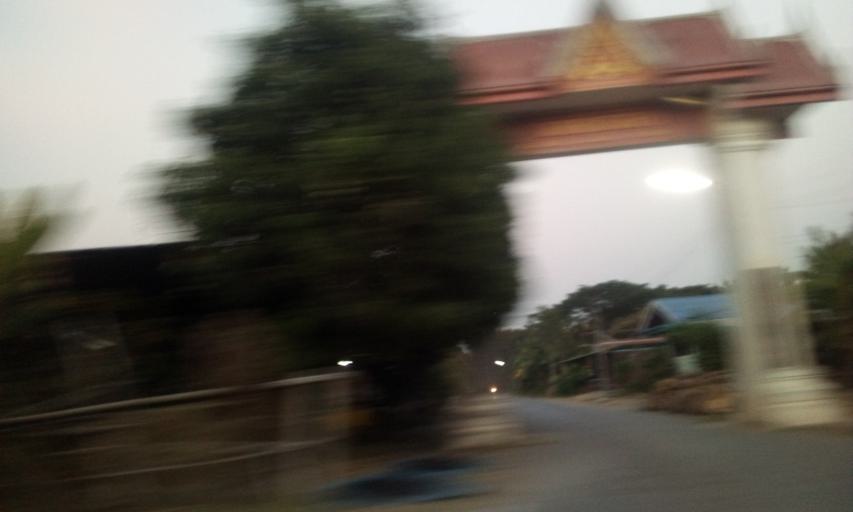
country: TH
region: Sing Buri
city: Sing Buri
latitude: 14.8284
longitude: 100.4048
